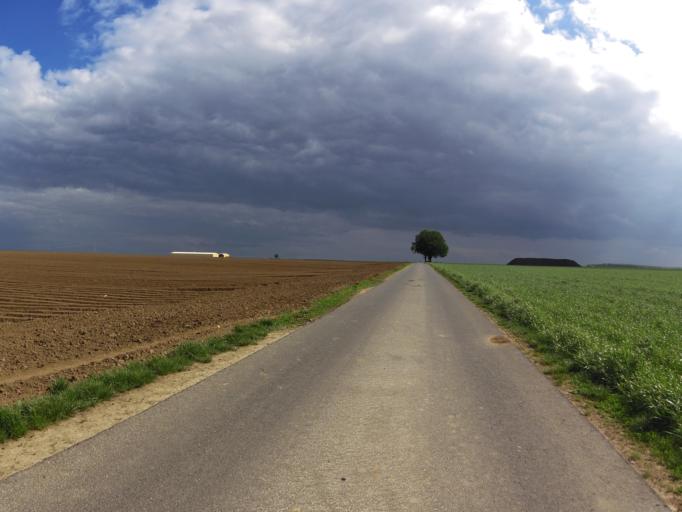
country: DE
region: Bavaria
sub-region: Regierungsbezirk Unterfranken
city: Oberpleichfeld
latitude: 49.8708
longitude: 10.0798
